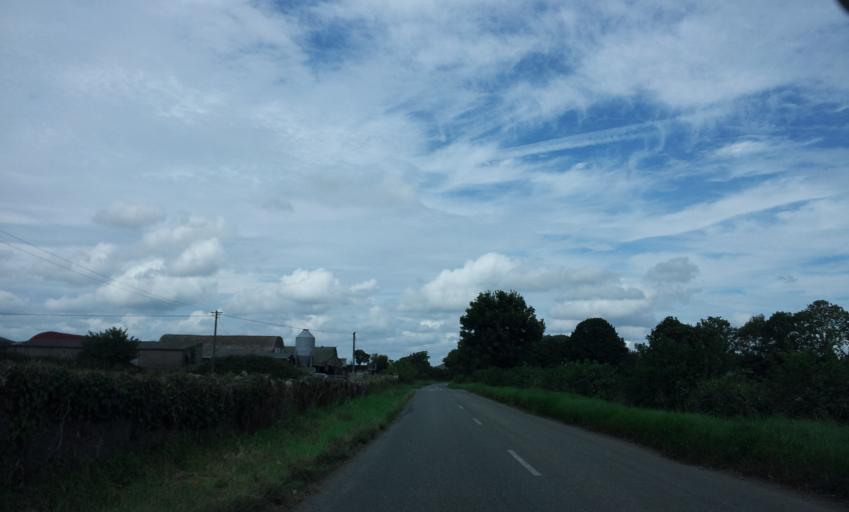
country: IE
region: Leinster
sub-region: Laois
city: Stradbally
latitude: 52.9782
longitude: -7.2153
